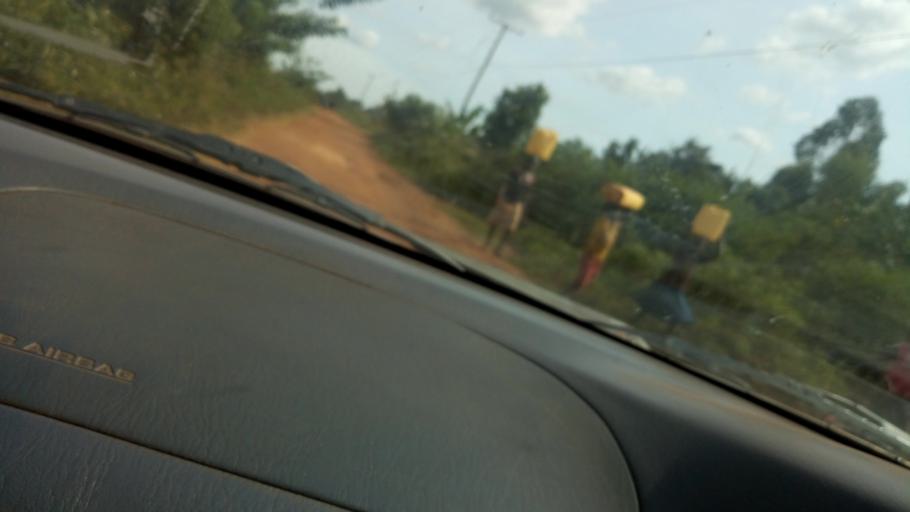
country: UG
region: Western Region
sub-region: Kiryandongo District
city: Kiryandongo
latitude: 1.8119
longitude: 31.9401
